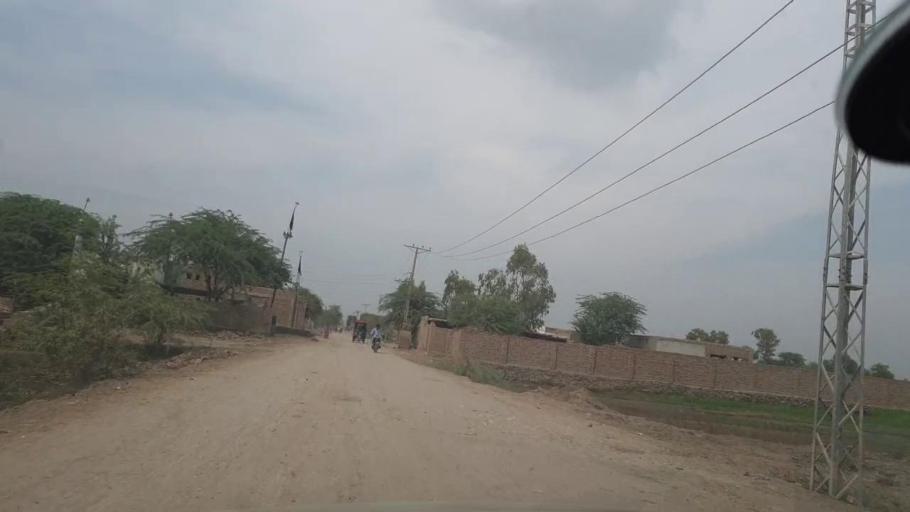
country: PK
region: Sindh
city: Jacobabad
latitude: 28.2631
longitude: 68.4375
